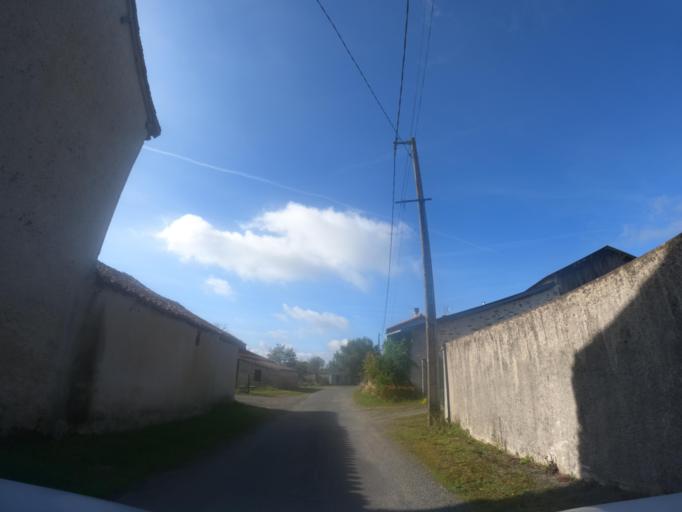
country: FR
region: Poitou-Charentes
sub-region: Departement des Deux-Sevres
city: Courlay
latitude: 46.7935
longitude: -0.5871
